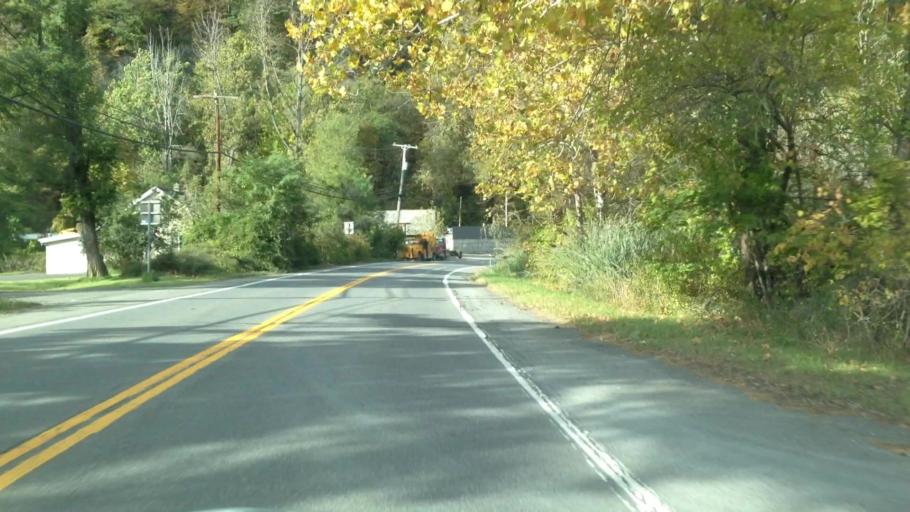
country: US
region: New York
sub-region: Ulster County
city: Kingston
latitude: 41.8973
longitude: -74.0209
